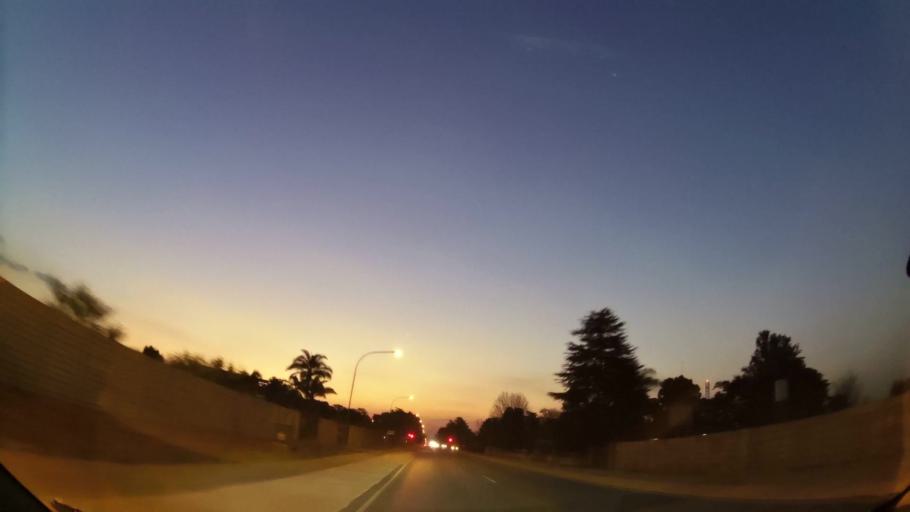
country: ZA
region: Gauteng
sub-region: Ekurhuleni Metropolitan Municipality
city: Benoni
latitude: -26.0918
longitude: 28.3035
